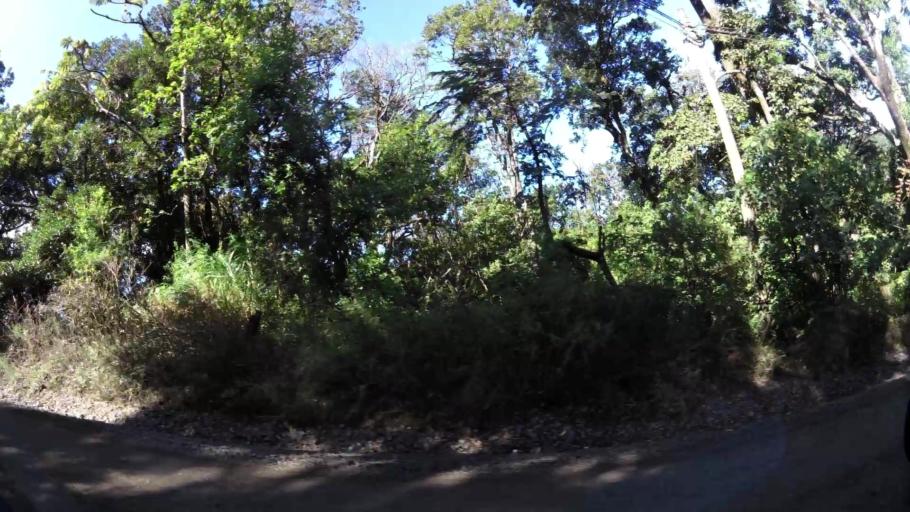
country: CR
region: Guanacaste
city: Juntas
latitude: 10.3272
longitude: -84.8378
